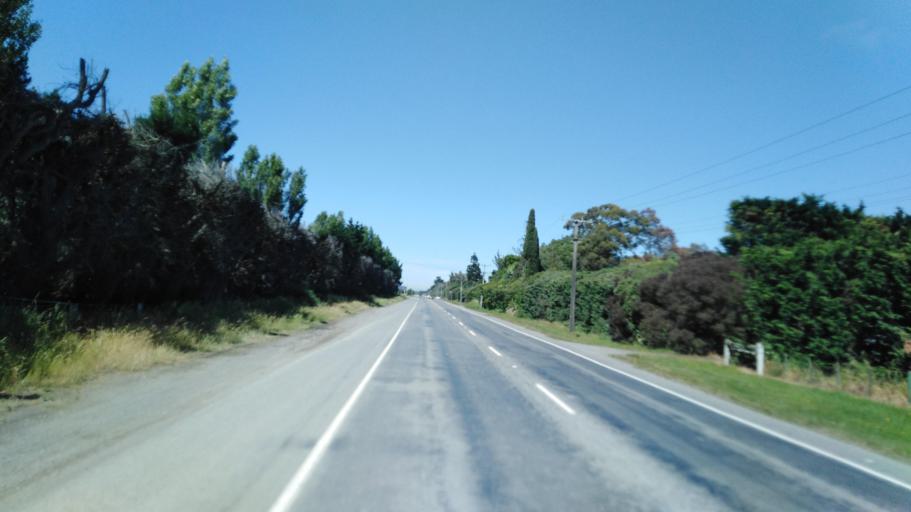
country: NZ
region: Canterbury
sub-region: Selwyn District
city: Prebbleton
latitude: -43.5309
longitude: 172.4983
